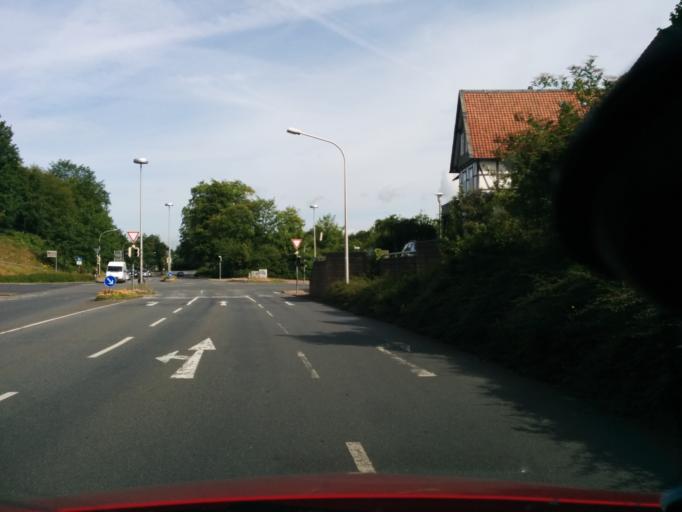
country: DE
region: Lower Saxony
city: Goslar
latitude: 51.9116
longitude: 10.4172
